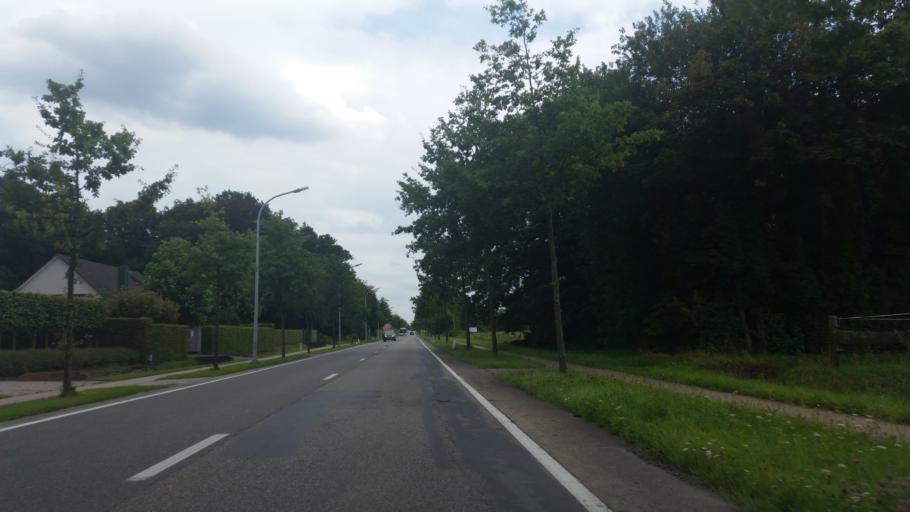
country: BE
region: Flanders
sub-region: Provincie Antwerpen
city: Merksplas
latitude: 51.3465
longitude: 4.8843
